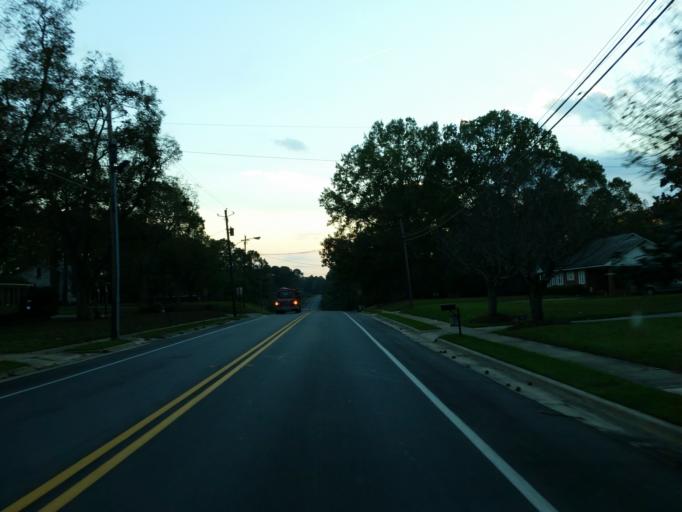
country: US
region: Georgia
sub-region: Pulaski County
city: Hawkinsville
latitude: 32.2766
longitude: -83.4768
